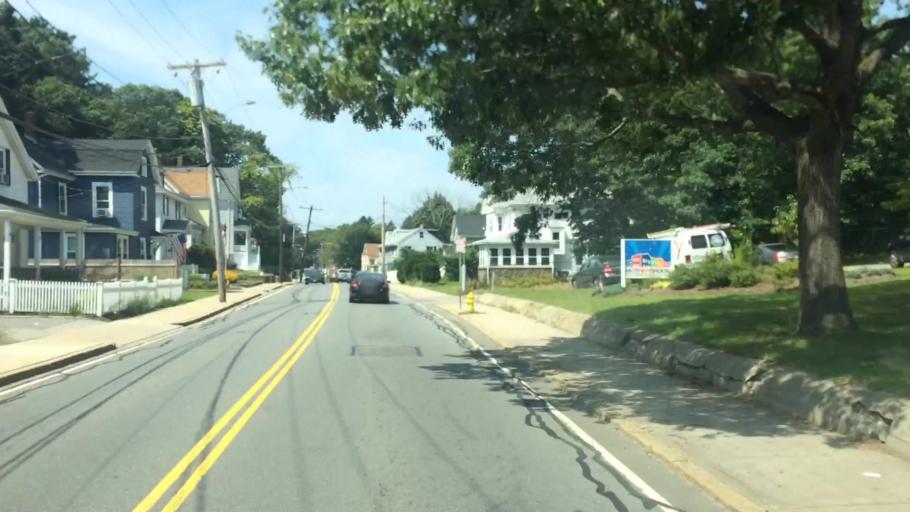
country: US
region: Massachusetts
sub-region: Norfolk County
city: Dedham
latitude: 42.2478
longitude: -71.1571
